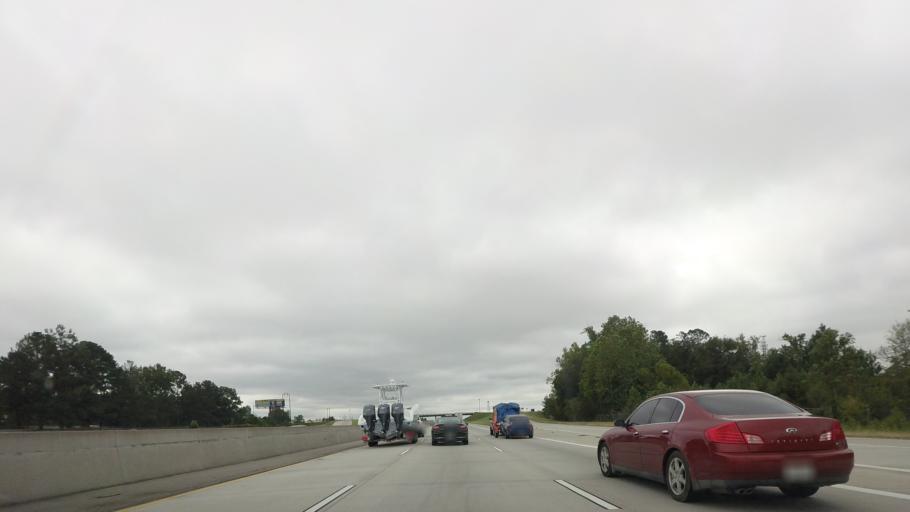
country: US
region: Georgia
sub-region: Cook County
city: Adel
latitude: 31.1155
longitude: -83.4294
